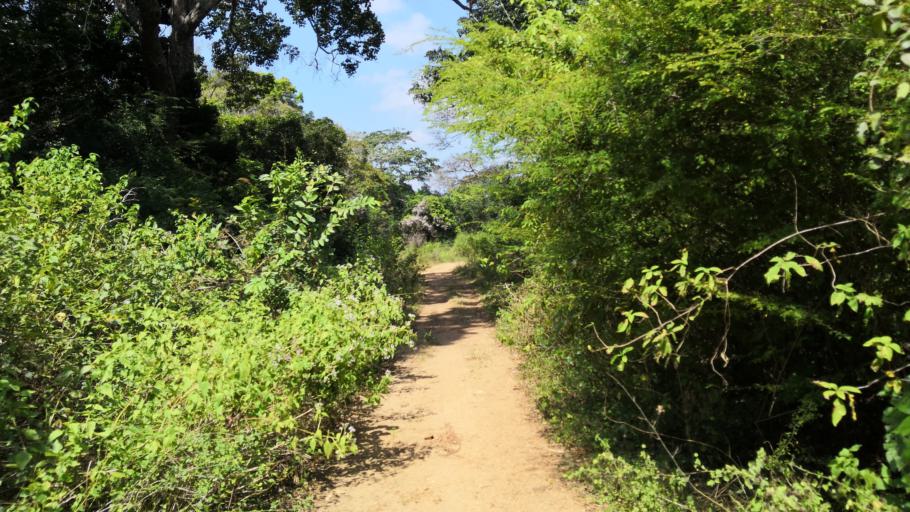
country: LK
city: Padaviya Divisional Secretariat
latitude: 8.9575
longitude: 80.6983
